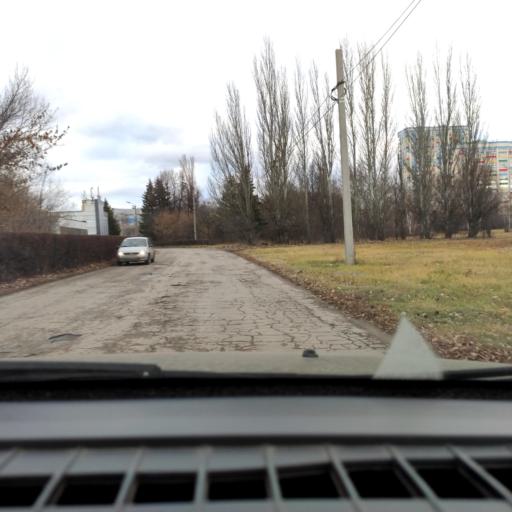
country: RU
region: Samara
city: Tol'yatti
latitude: 53.5437
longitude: 49.2976
